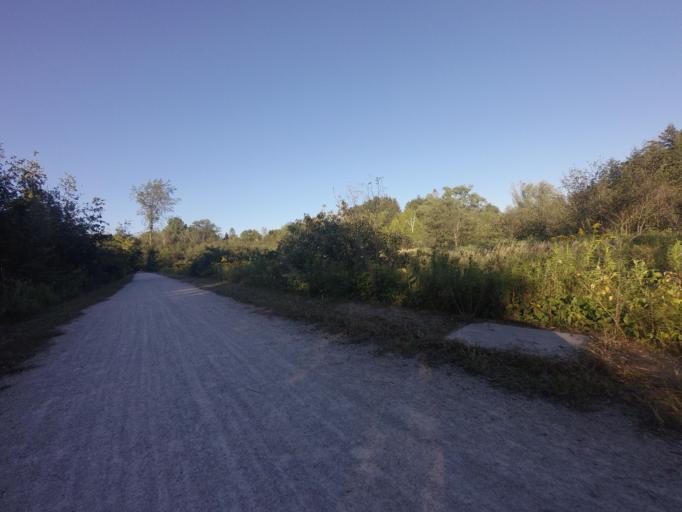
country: CA
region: Ontario
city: Orangeville
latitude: 43.8204
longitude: -79.9225
